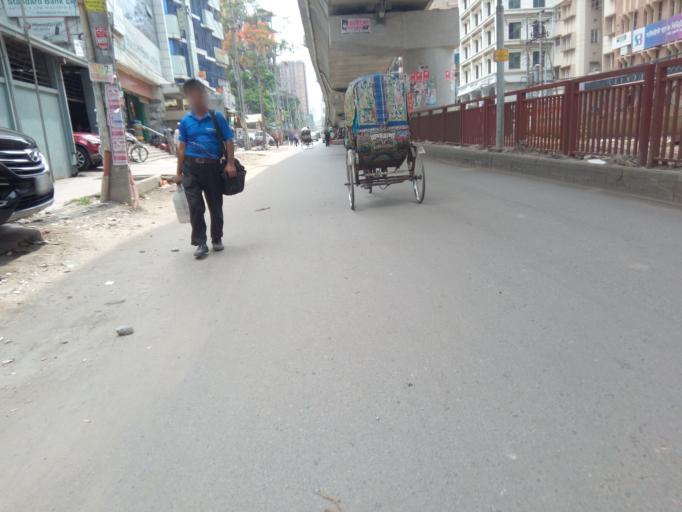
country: BD
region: Dhaka
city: Paltan
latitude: 23.7473
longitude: 90.4002
